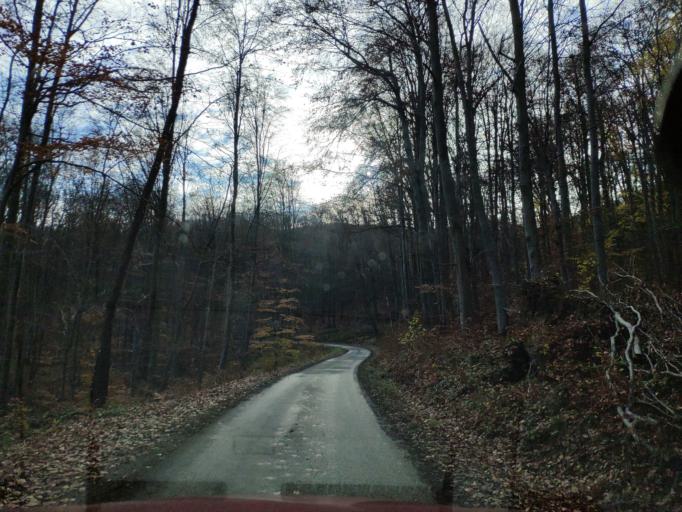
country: HU
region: Borsod-Abauj-Zemplen
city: Gonc
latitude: 48.5827
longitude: 21.4724
